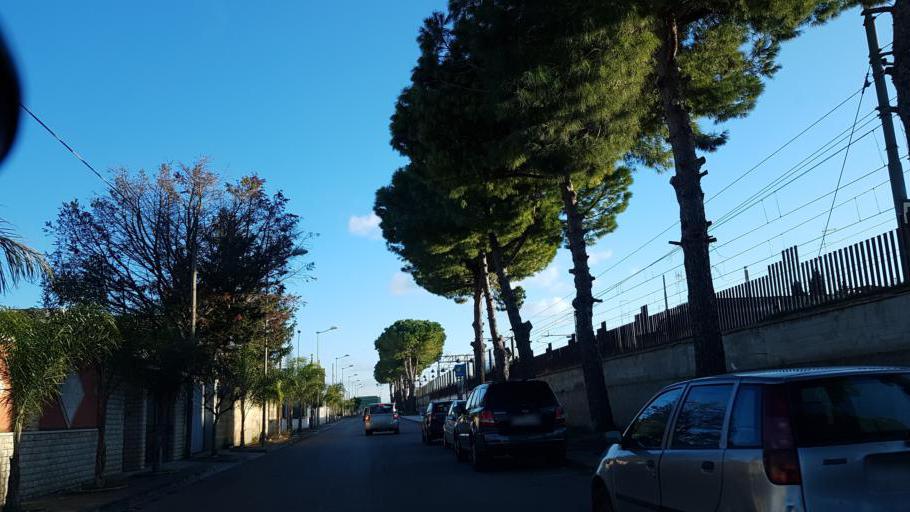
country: IT
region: Apulia
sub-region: Provincia di Lecce
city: Squinzano
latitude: 40.4359
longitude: 18.0499
